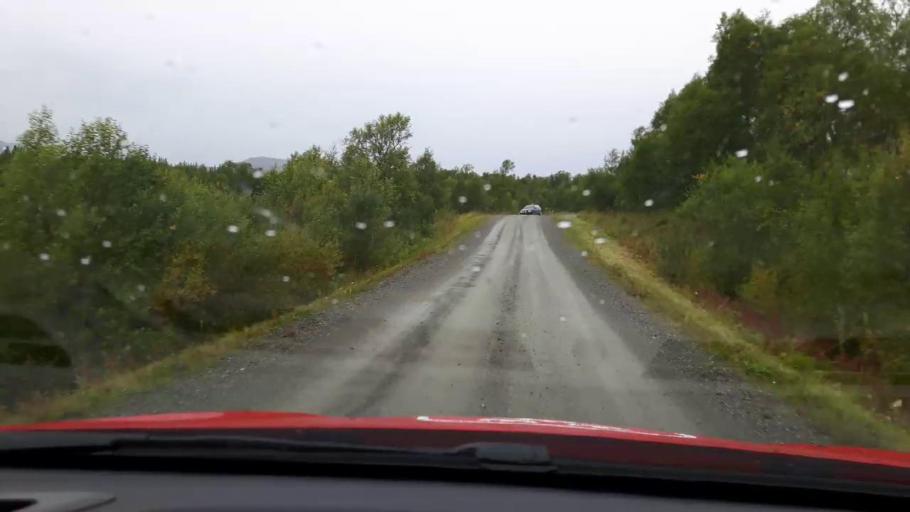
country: NO
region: Nord-Trondelag
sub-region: Meraker
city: Meraker
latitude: 63.5706
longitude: 12.2810
